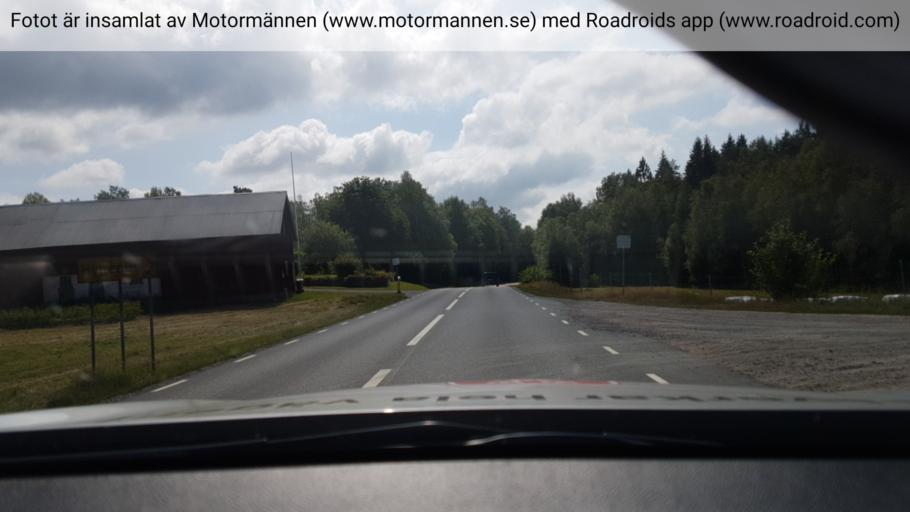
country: SE
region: Vaestra Goetaland
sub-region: Marks Kommun
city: Fritsla
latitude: 57.4752
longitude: 12.7735
